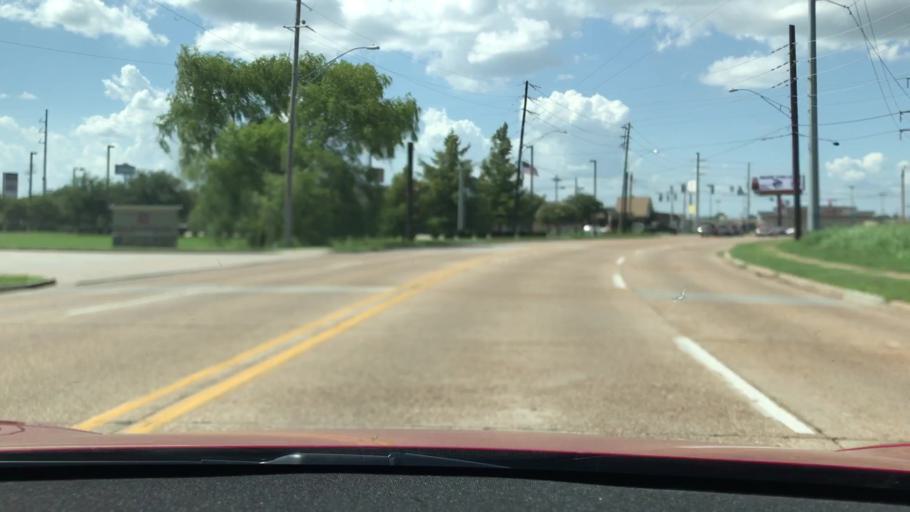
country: US
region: Louisiana
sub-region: Bossier Parish
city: Bossier City
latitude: 32.4421
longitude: -93.7134
